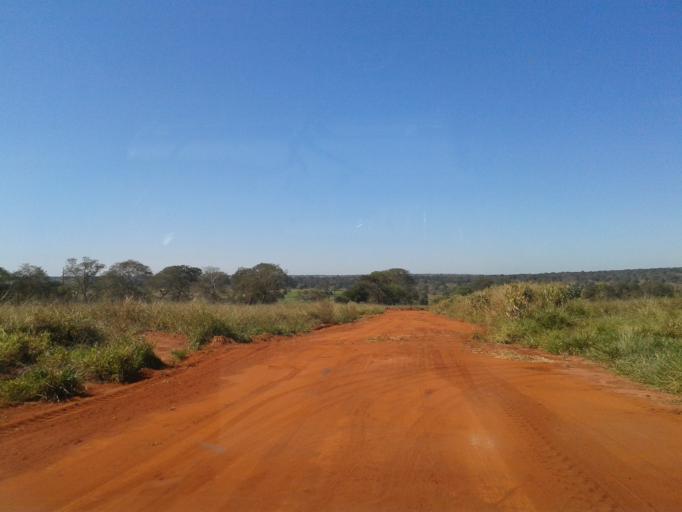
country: BR
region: Minas Gerais
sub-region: Santa Vitoria
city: Santa Vitoria
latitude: -18.8631
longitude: -50.1194
